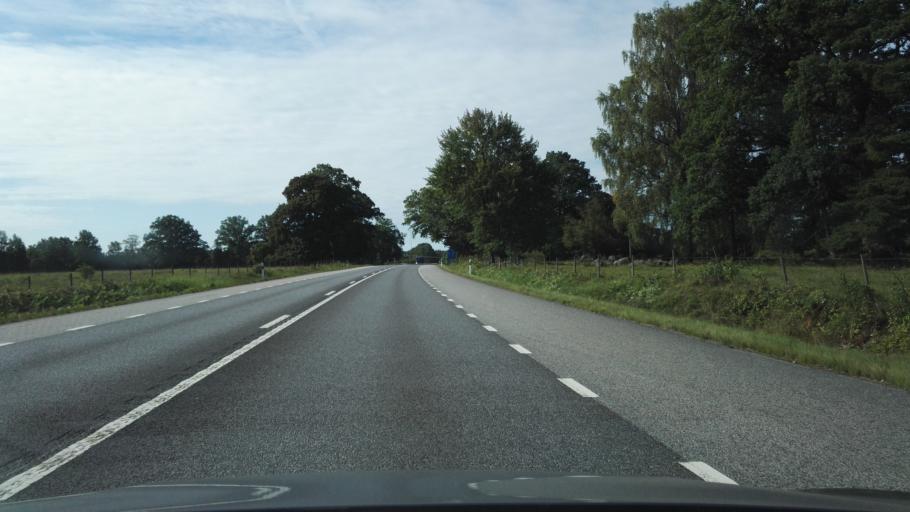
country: SE
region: Kronoberg
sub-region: Vaxjo Kommun
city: Vaexjoe
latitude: 56.8697
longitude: 14.7396
